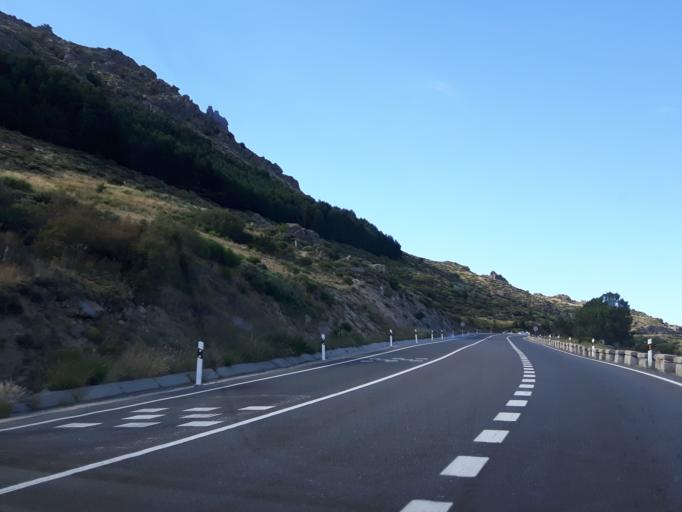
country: ES
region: Castille and Leon
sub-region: Provincia de Avila
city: Mengamunoz
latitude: 40.4866
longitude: -5.0057
